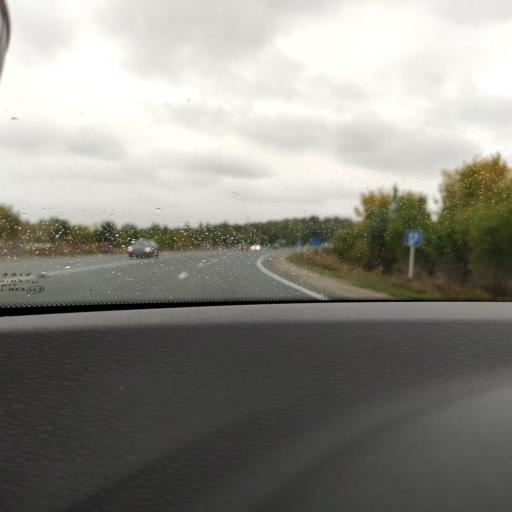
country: RU
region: Samara
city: Mirnyy
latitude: 53.6063
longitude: 50.2741
